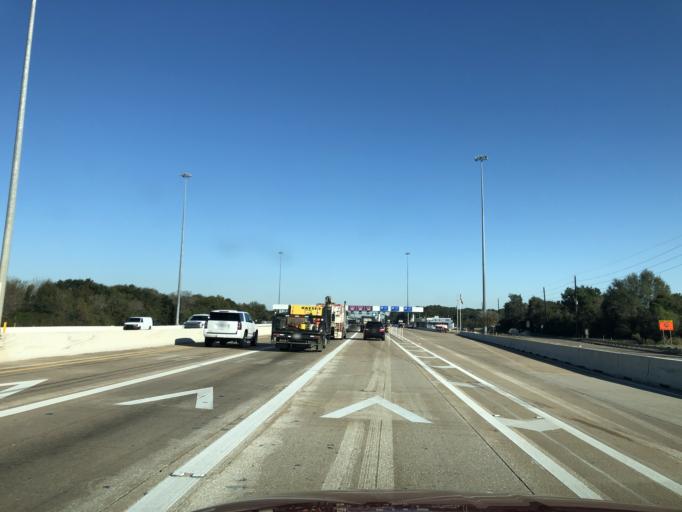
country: US
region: Texas
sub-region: Fort Bend County
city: Fresno
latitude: 29.5964
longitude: -95.4136
